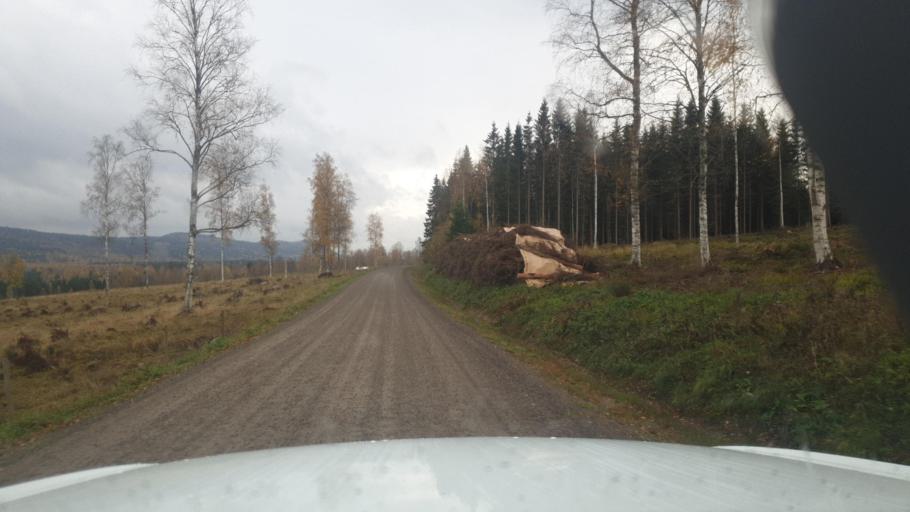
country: SE
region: Vaermland
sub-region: Torsby Kommun
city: Torsby
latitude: 59.9527
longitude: 12.8941
